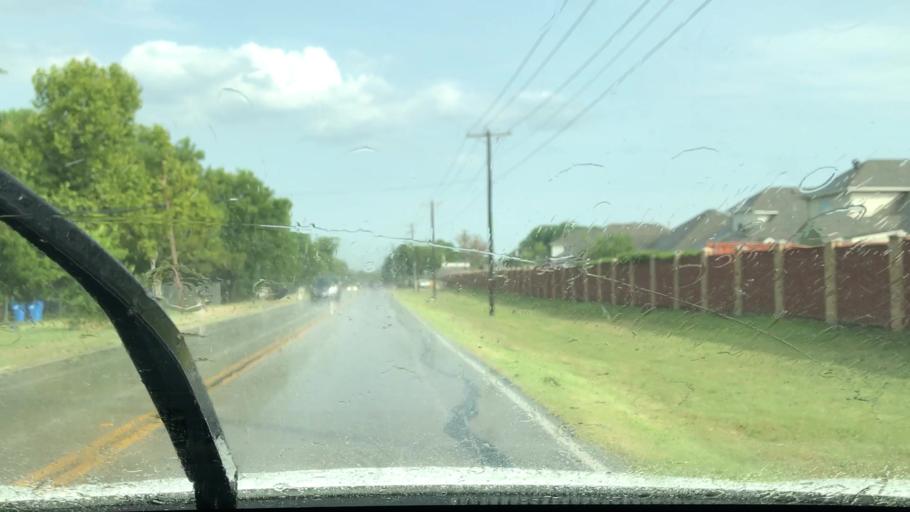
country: US
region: Texas
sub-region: Collin County
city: Wylie
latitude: 32.9590
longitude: -96.5297
